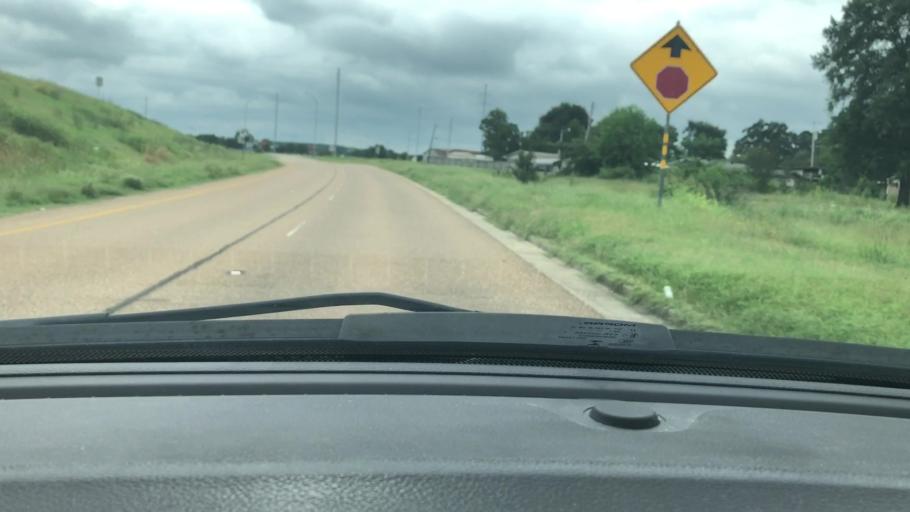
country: US
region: Texas
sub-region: Bowie County
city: Wake Village
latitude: 33.3870
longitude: -94.0942
